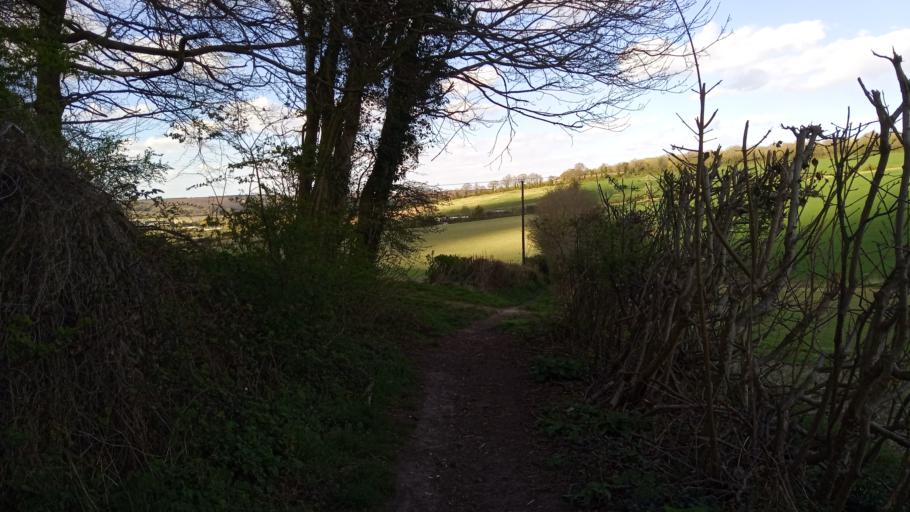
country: GB
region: England
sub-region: Kent
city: Chartham
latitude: 51.2490
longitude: 1.0348
